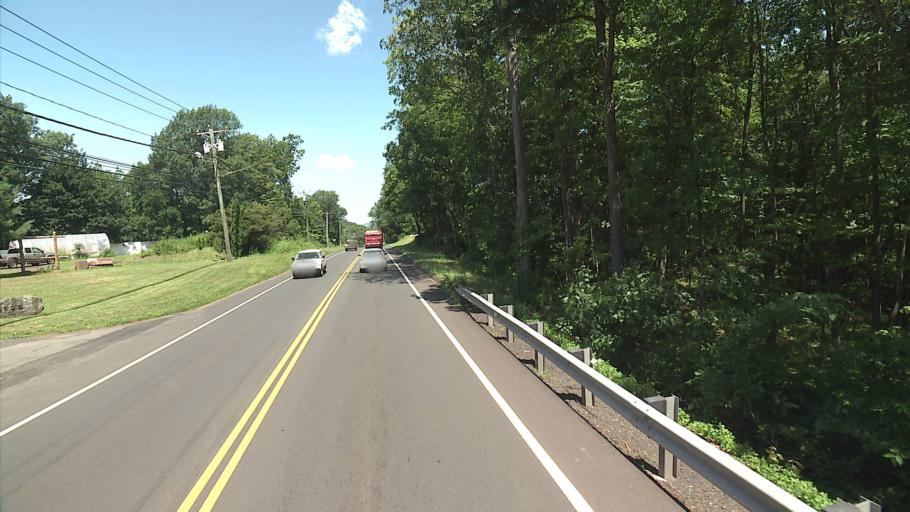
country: US
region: Connecticut
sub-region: Hartford County
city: Kensington
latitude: 41.6128
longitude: -72.7239
